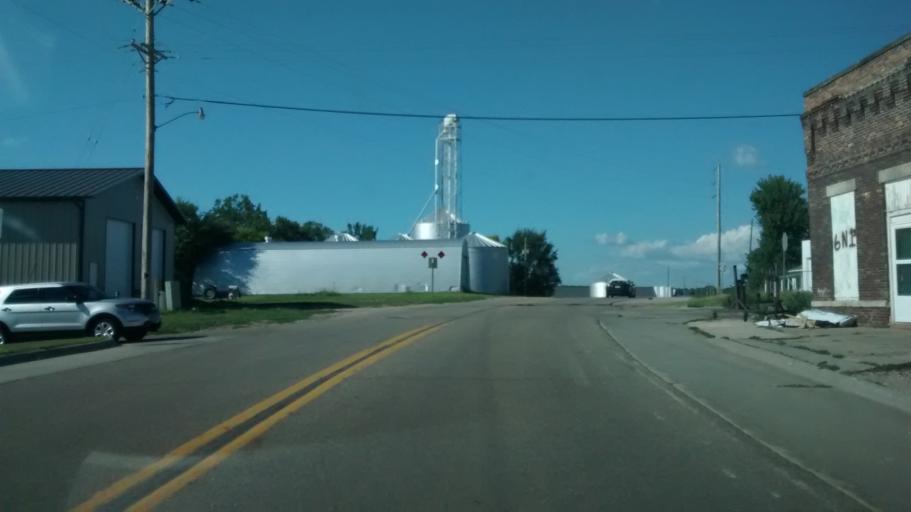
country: US
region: Iowa
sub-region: Woodbury County
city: Moville
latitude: 42.4890
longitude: -96.0751
